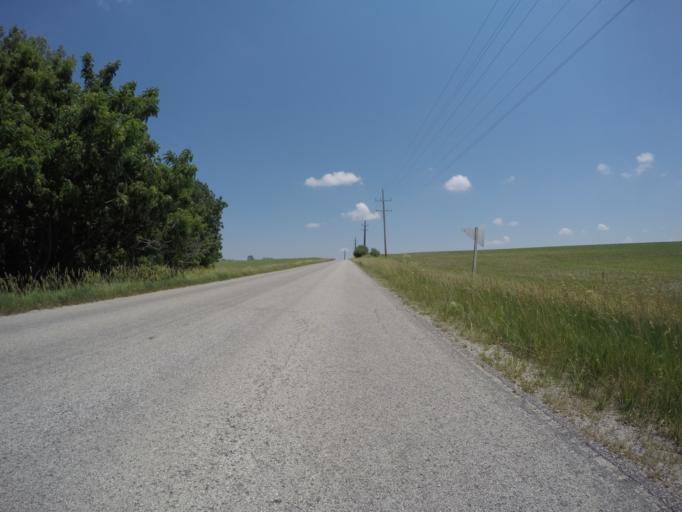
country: US
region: Kansas
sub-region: Doniphan County
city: Troy
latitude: 39.7677
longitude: -95.1231
